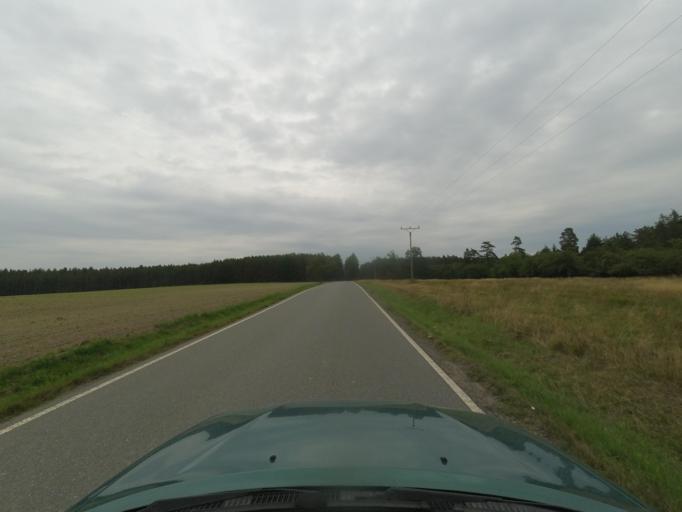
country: CZ
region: Plzensky
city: Stankov
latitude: 49.5455
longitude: 13.1191
